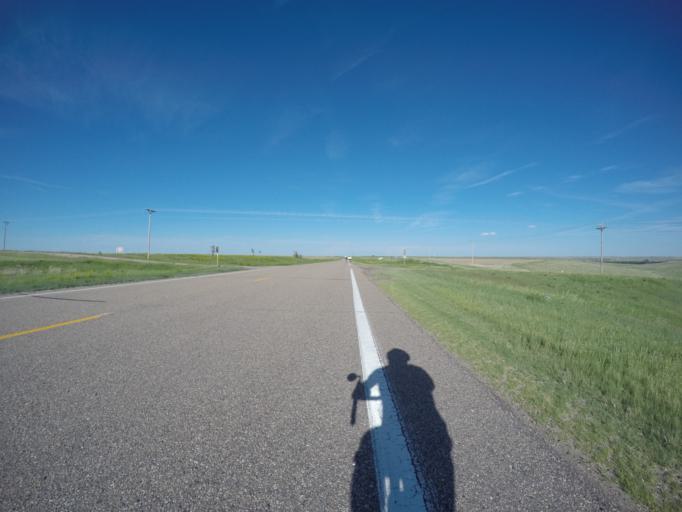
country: US
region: Kansas
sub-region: Cheyenne County
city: Saint Francis
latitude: 39.7570
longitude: -101.9002
